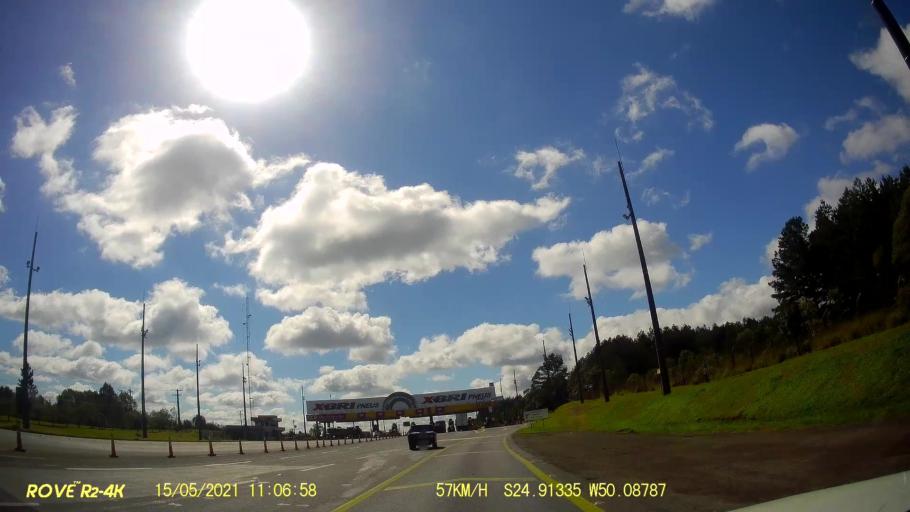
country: BR
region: Parana
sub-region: Carambei
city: Carambei
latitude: -24.9135
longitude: -50.0880
